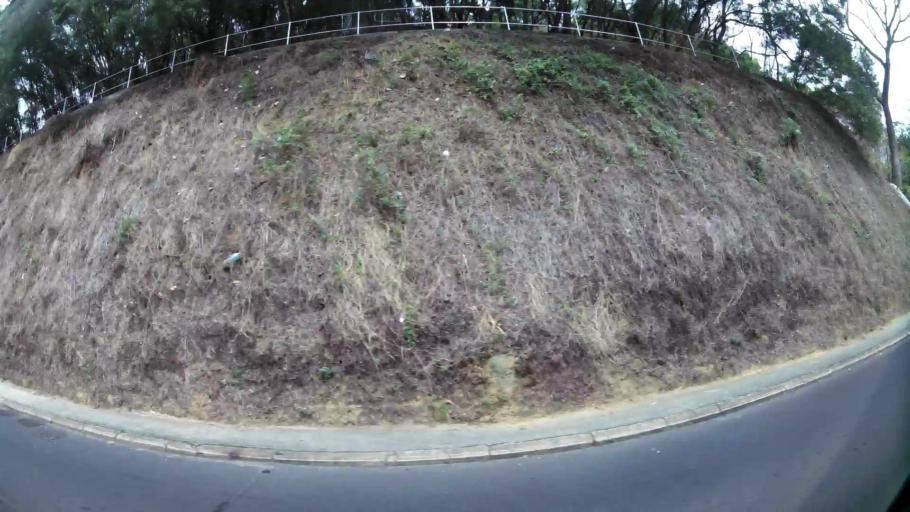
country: HK
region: Sham Shui Po
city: Sham Shui Po
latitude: 22.3366
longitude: 114.1620
